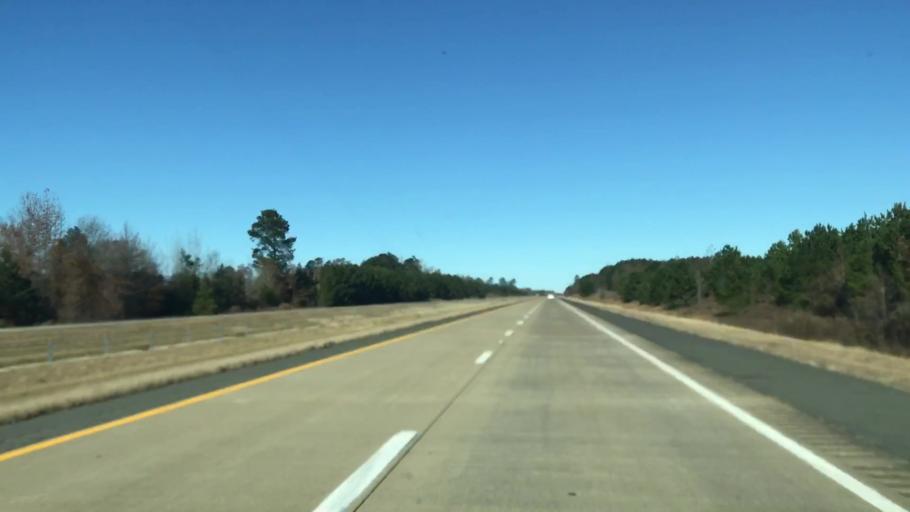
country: US
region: Texas
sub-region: Bowie County
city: Texarkana
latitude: 33.3029
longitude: -93.9319
